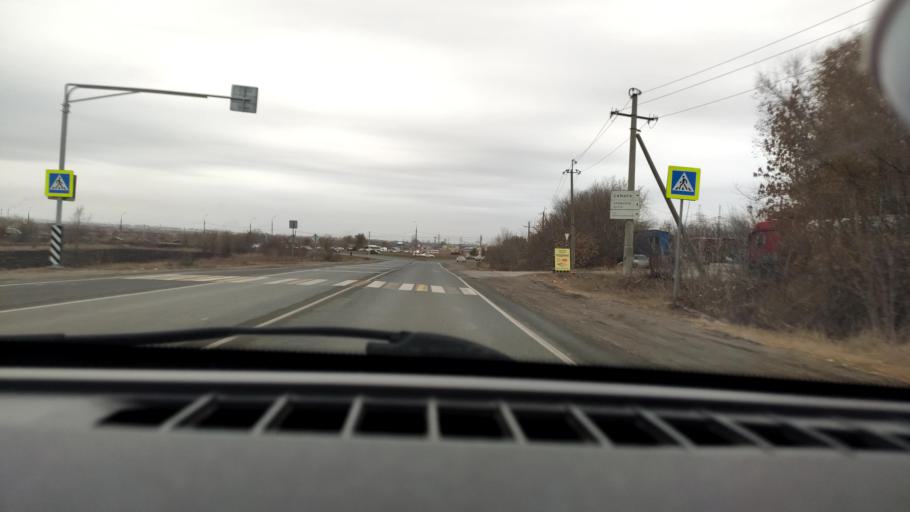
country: RU
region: Samara
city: Samara
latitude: 53.1261
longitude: 50.1747
